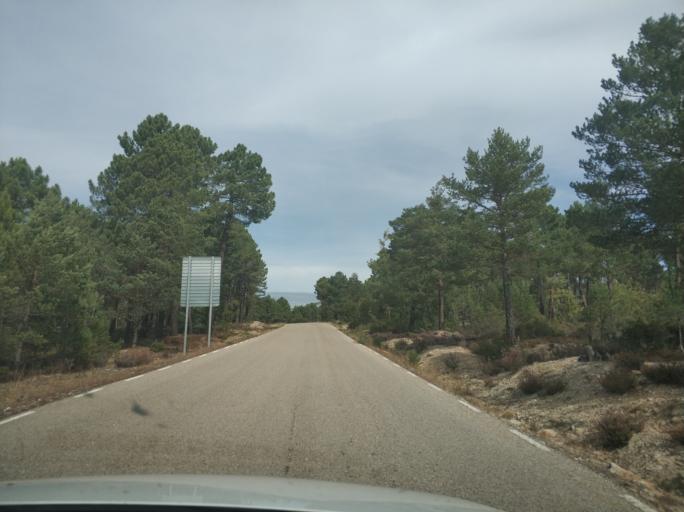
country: ES
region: Castille and Leon
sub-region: Provincia de Soria
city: Duruelo de la Sierra
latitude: 41.8818
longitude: -2.9364
